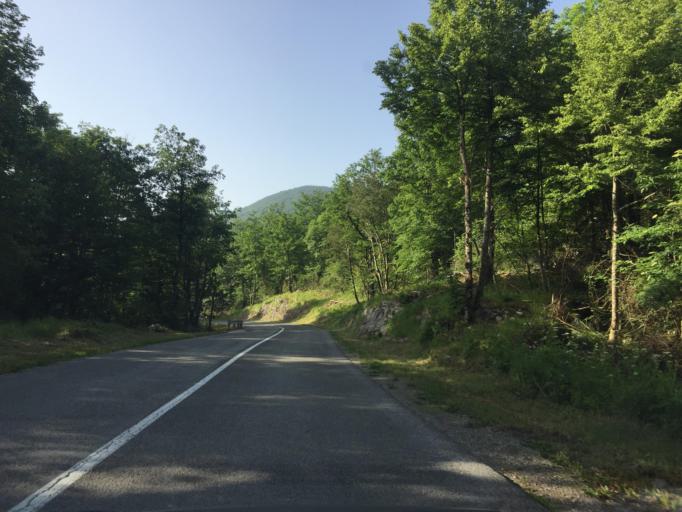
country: HR
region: Primorsko-Goranska
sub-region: Grad Opatija
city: Opatija
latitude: 45.4312
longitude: 14.2026
